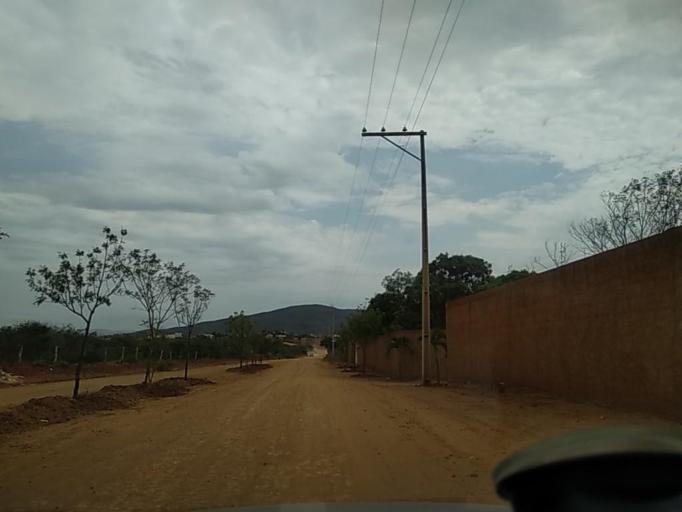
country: BR
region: Bahia
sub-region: Caetite
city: Caetite
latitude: -14.0468
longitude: -42.4735
